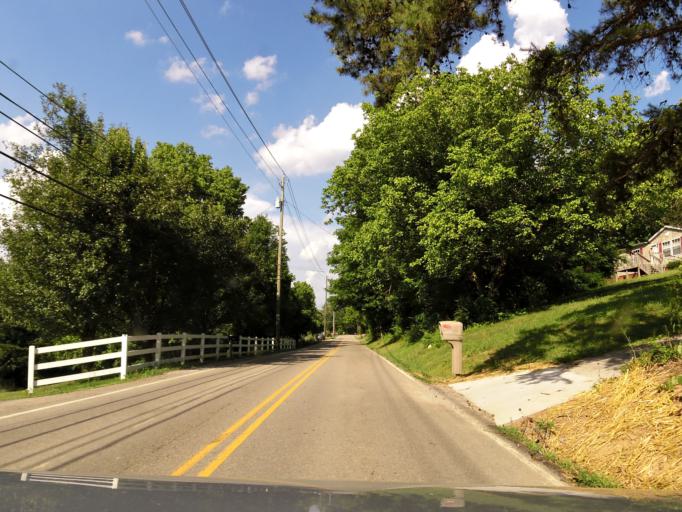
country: US
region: Tennessee
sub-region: Knox County
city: Knoxville
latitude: 36.0724
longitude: -83.8914
